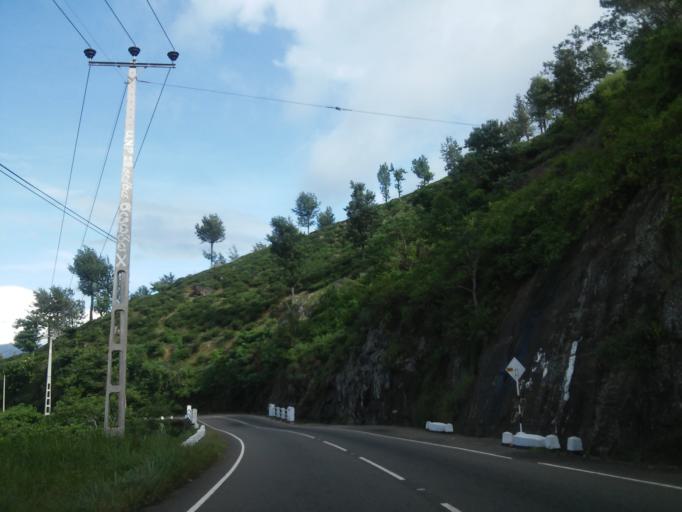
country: LK
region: Uva
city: Haputale
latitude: 6.7614
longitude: 80.9331
